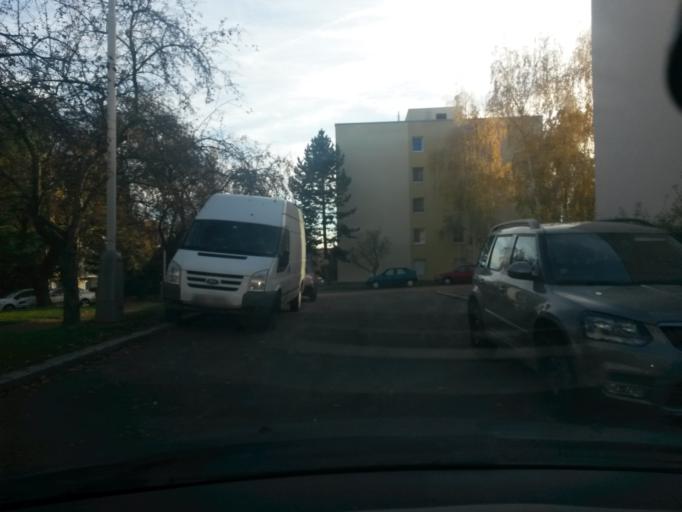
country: CZ
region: Central Bohemia
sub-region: Okres Praha-Zapad
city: Pruhonice
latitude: 50.0300
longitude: 14.5379
